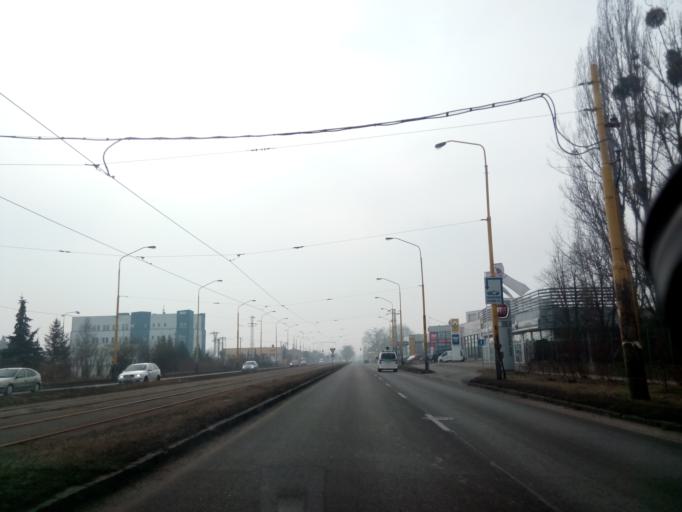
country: SK
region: Kosicky
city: Kosice
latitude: 48.6818
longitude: 21.2679
